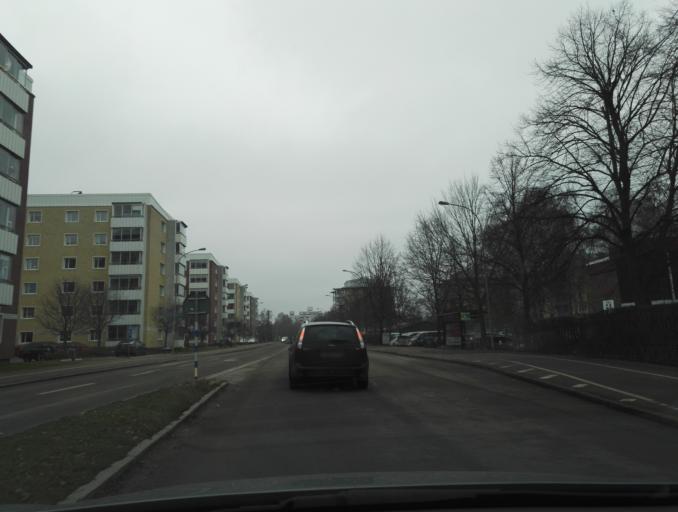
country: SE
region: Kronoberg
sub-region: Vaxjo Kommun
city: Vaexjoe
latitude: 56.8821
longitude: 14.8002
